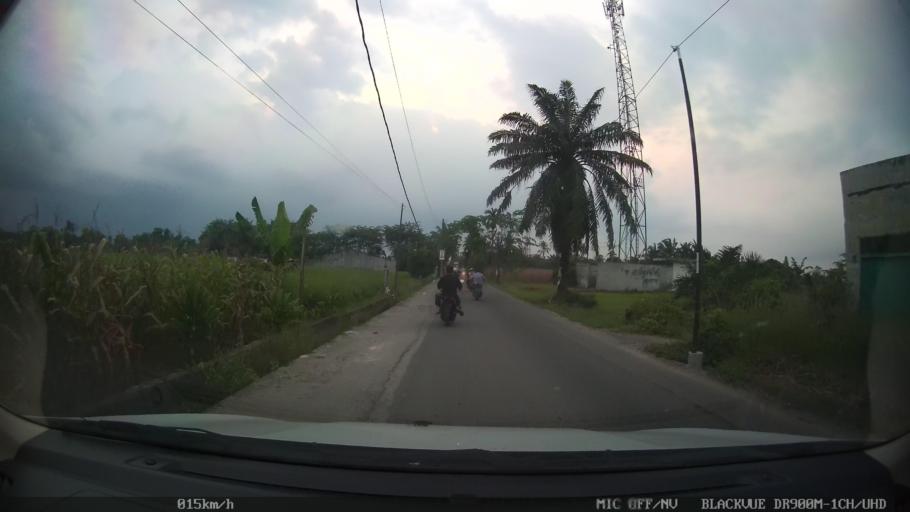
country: ID
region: North Sumatra
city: Sunggal
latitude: 3.5610
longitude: 98.5896
